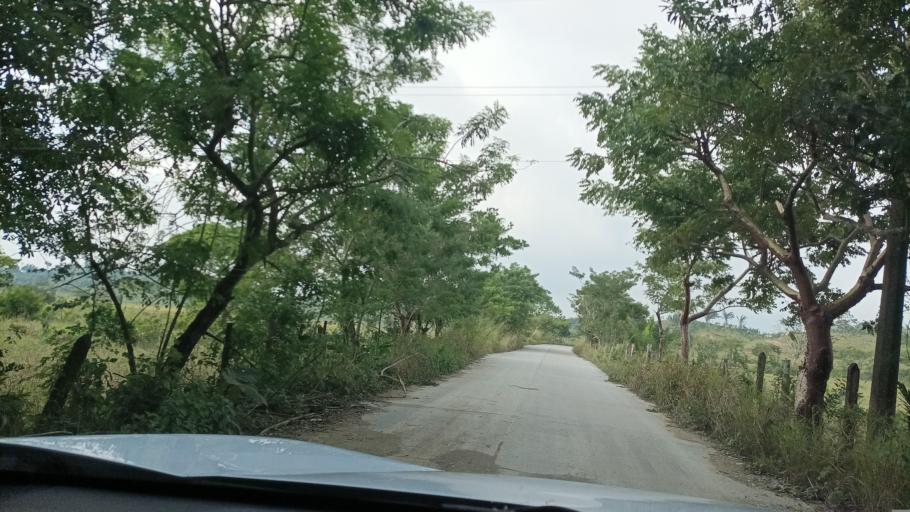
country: MX
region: Veracruz
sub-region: Moloacan
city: Tlacuilolapan
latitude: 18.0777
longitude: -94.2883
